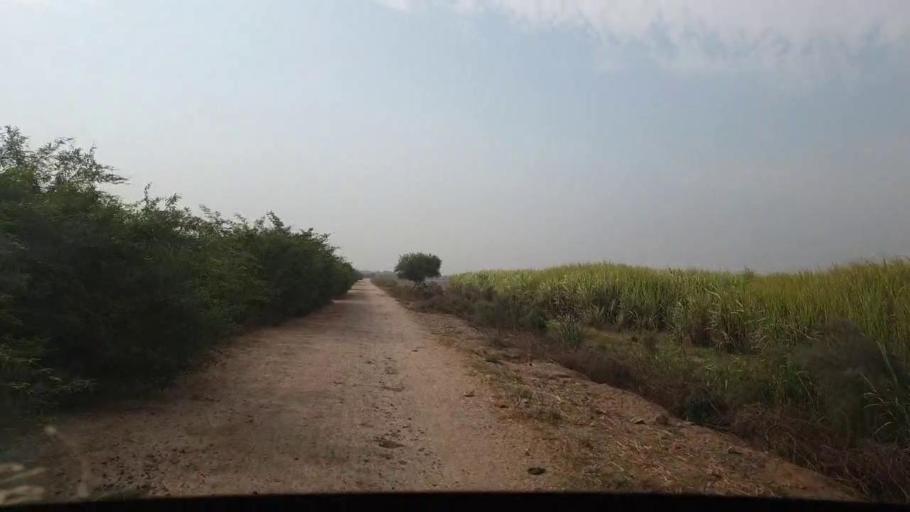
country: PK
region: Sindh
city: Chuhar Jamali
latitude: 24.4123
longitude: 67.9386
